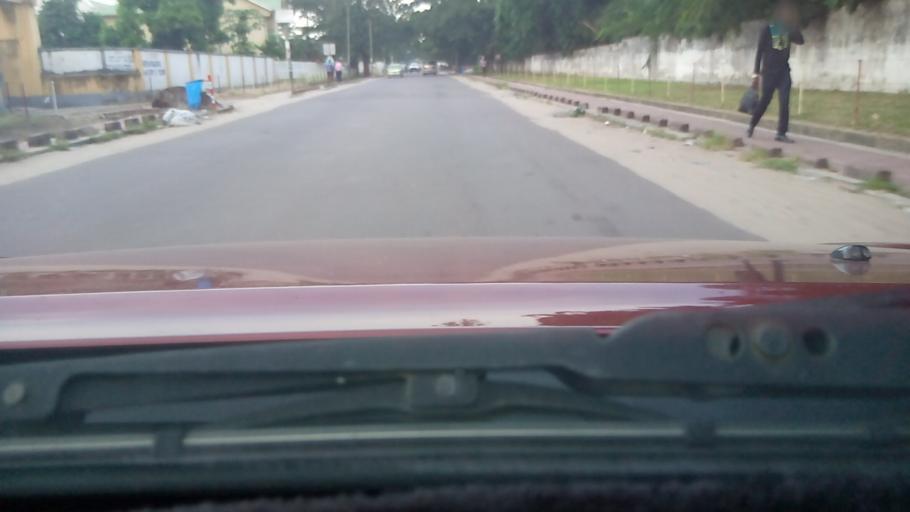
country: CD
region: Kinshasa
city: Kinshasa
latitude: -4.3090
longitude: 15.2837
